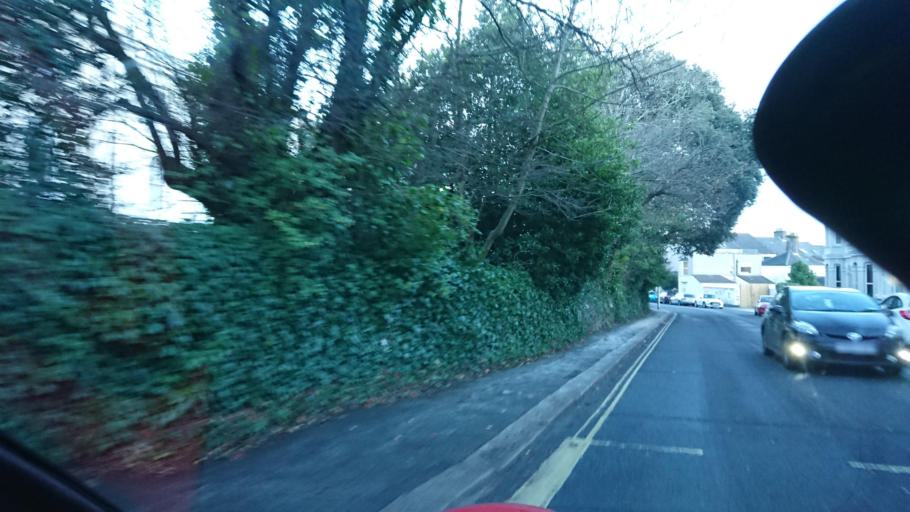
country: GB
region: England
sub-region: Plymouth
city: Plymouth
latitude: 50.3781
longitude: -4.1243
